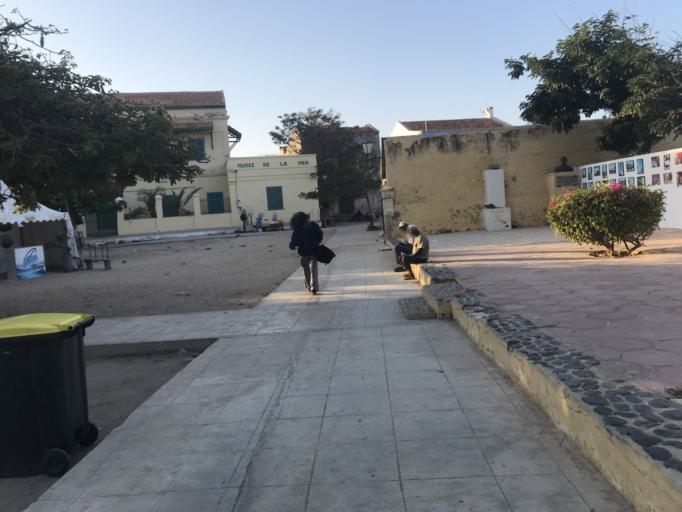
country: SN
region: Dakar
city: Dakar
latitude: 14.6683
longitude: -17.3994
